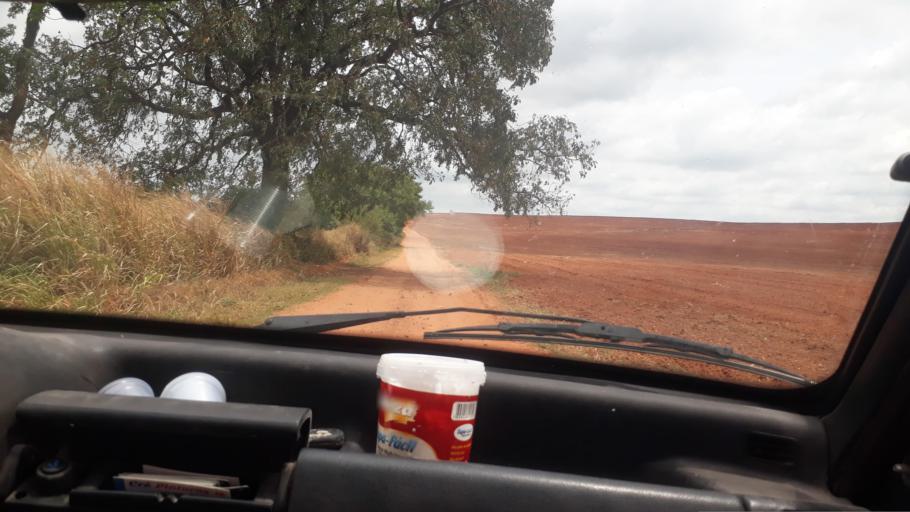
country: BR
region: Sao Paulo
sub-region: Regente Feijo
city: Regente Feijo
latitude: -22.2575
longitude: -51.3010
